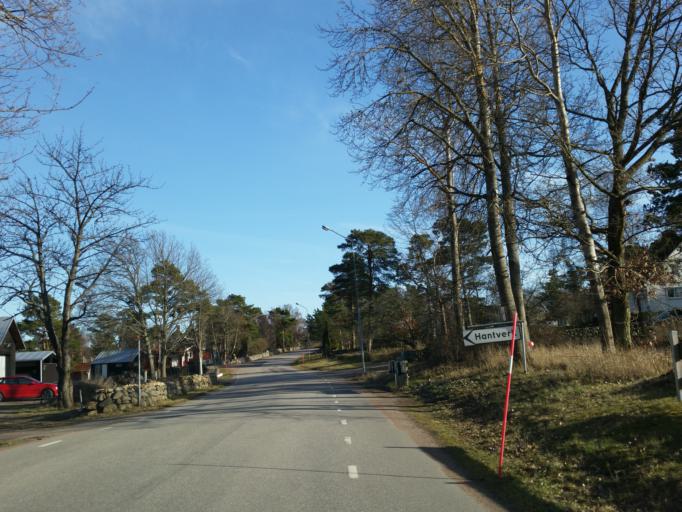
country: SE
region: Kalmar
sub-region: Kalmar Kommun
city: Lindsdal
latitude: 56.7814
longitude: 16.4091
